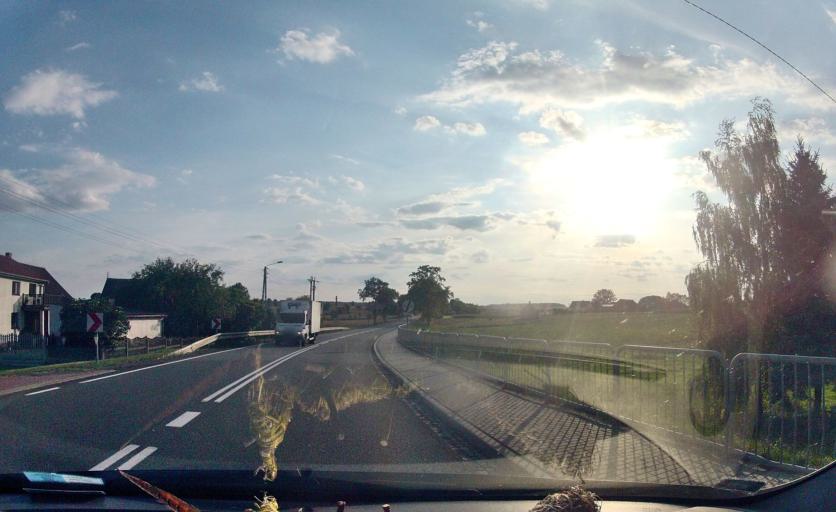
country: PL
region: Opole Voivodeship
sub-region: Powiat oleski
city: Gorzow Slaski
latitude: 51.0141
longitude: 18.3817
